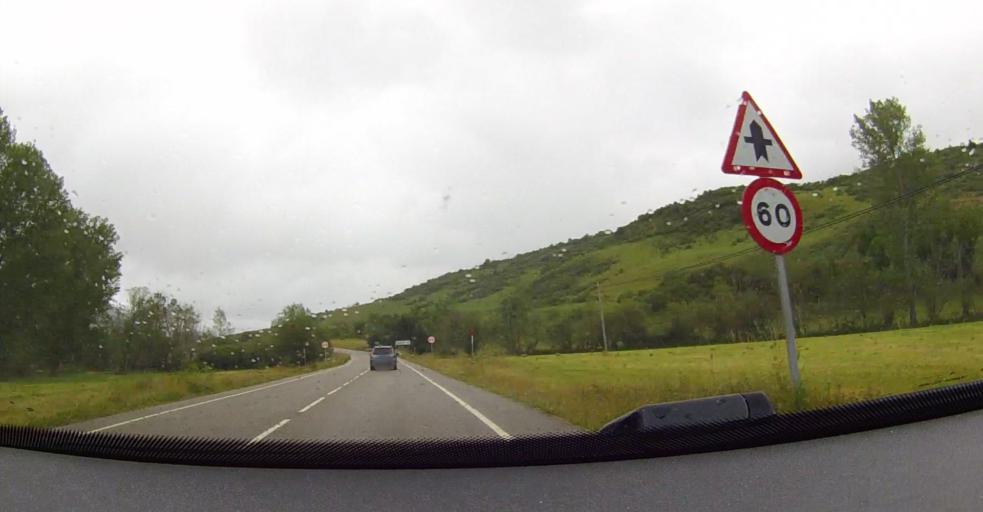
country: ES
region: Castille and Leon
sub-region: Provincia de Leon
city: Acebedo
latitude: 43.0454
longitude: -5.1250
